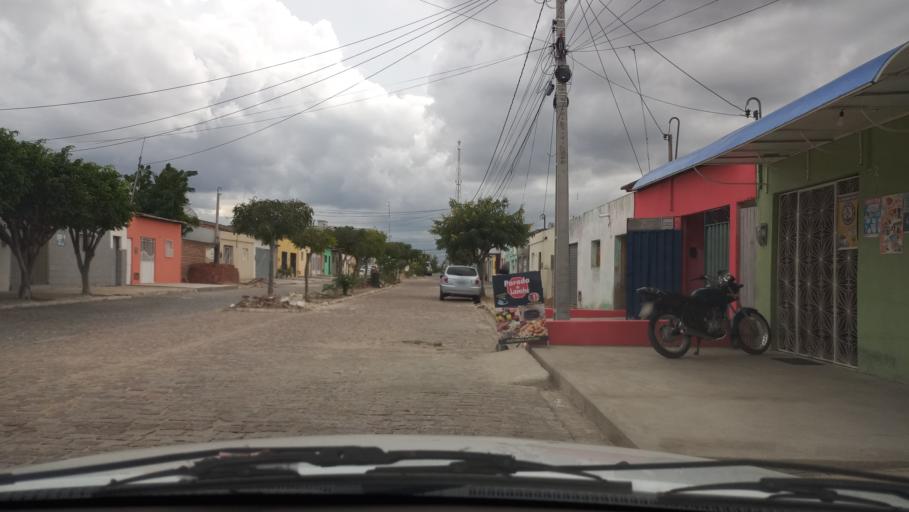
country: BR
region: Rio Grande do Norte
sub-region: Tangara
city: Tangara
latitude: -6.1955
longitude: -35.7979
